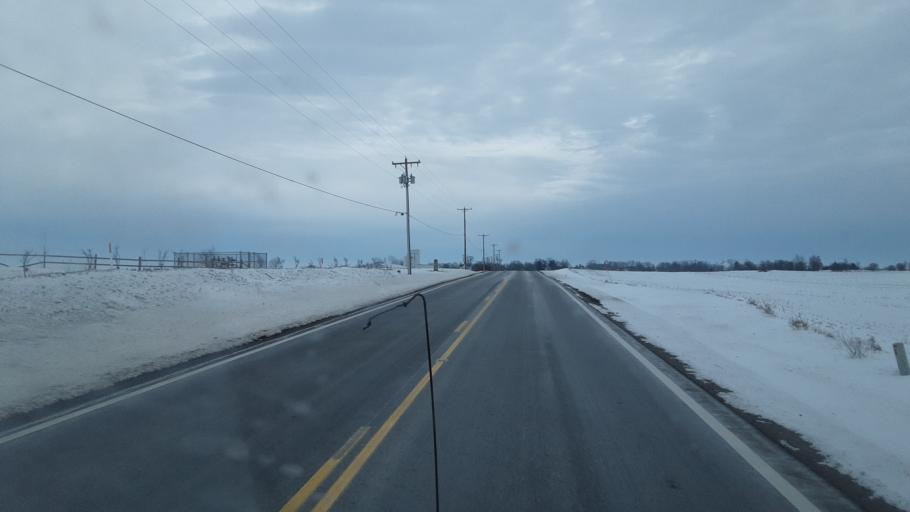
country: US
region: Ohio
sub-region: Madison County
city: Bethel
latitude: 39.7438
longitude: -83.4798
